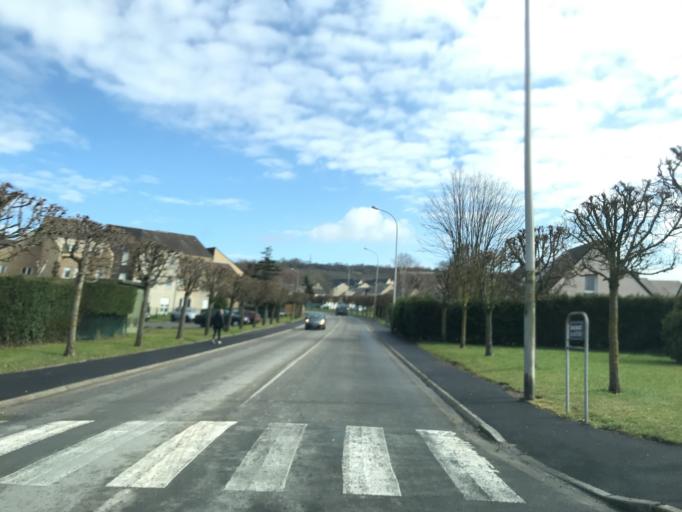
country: FR
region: Lower Normandy
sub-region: Departement du Calvados
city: Dives-sur-Mer
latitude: 49.2832
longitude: -0.0973
